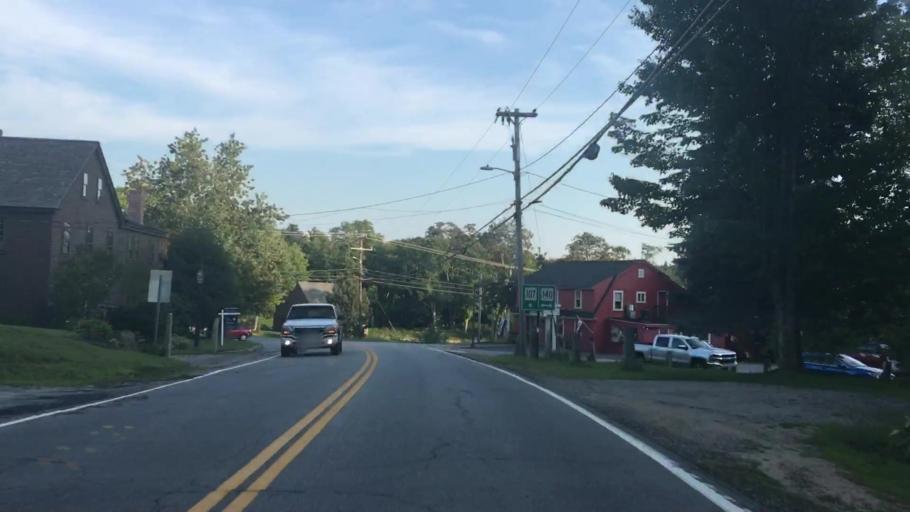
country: US
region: New Hampshire
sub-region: Belknap County
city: Gilmanton
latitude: 43.4247
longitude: -71.4139
